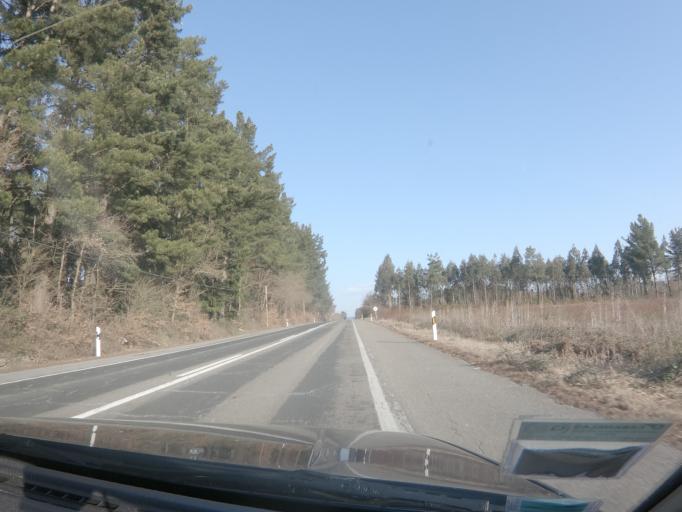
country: ES
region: Galicia
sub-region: Provincia de Lugo
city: Corgo
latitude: 42.9381
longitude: -7.4152
